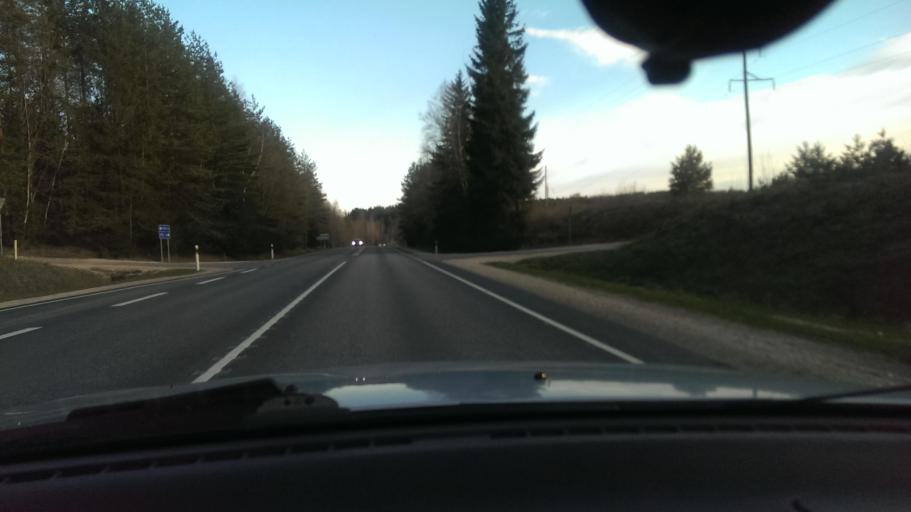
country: EE
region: Vorumaa
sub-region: Antsla vald
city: Vana-Antsla
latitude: 58.0074
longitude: 26.7566
